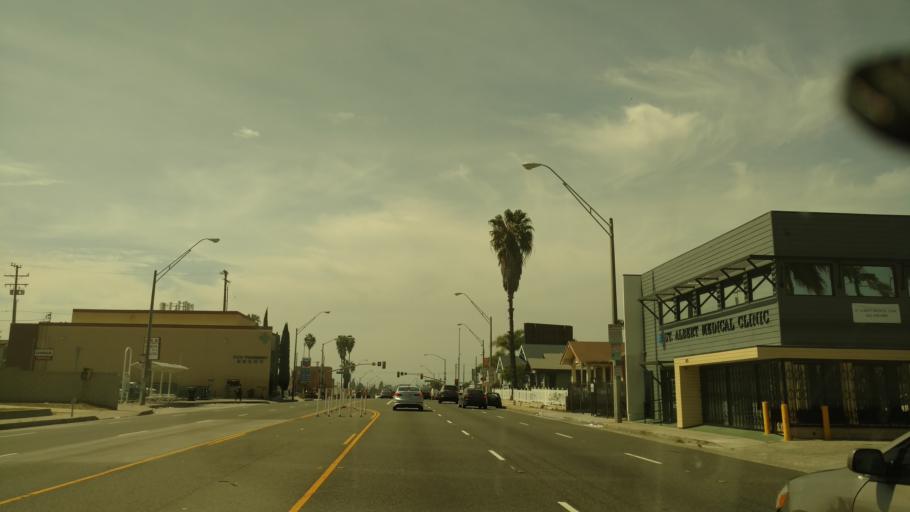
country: US
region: California
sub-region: Los Angeles County
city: Long Beach
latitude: 33.7898
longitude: -118.1876
